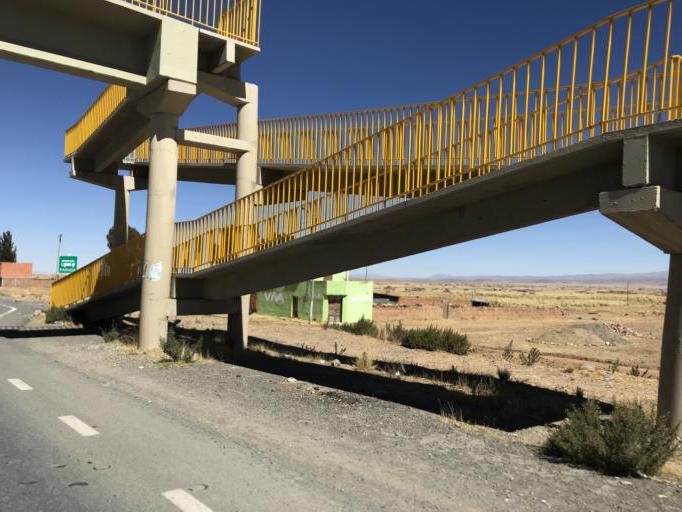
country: BO
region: La Paz
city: Batallas
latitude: -16.3967
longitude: -68.3625
